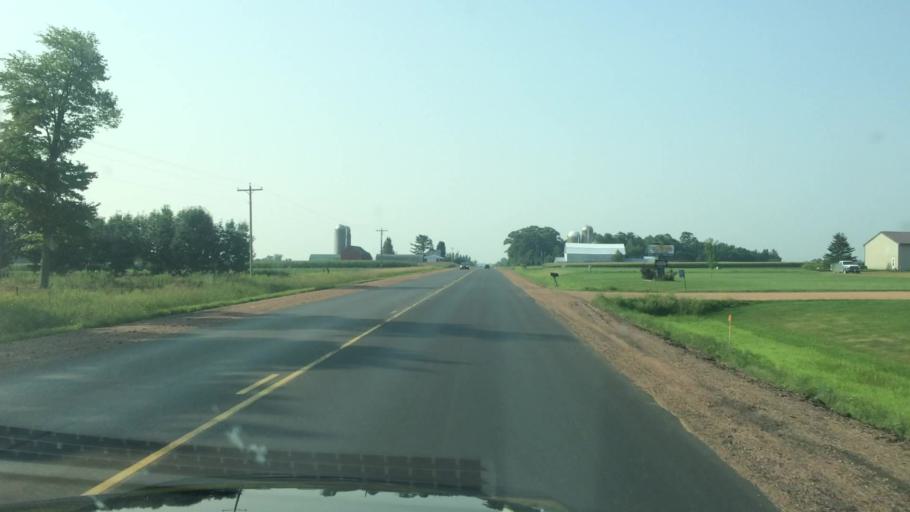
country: US
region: Wisconsin
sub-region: Marathon County
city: Stratford
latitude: 44.8561
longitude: -90.0792
